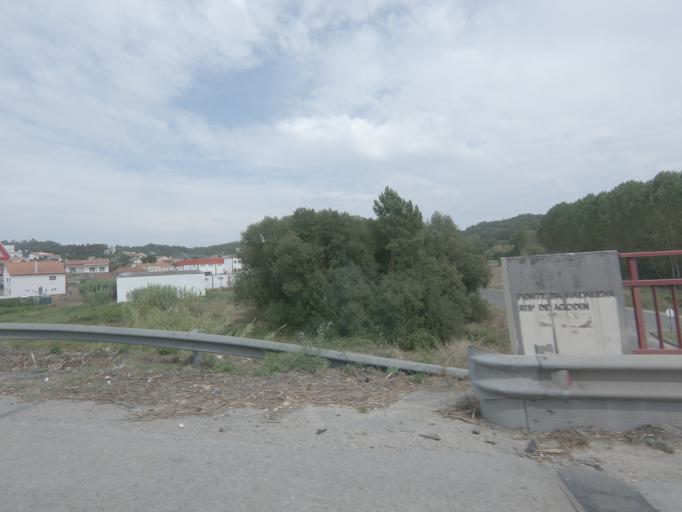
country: PT
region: Leiria
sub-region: Leiria
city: Caranguejeira
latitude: 39.8062
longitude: -8.7419
